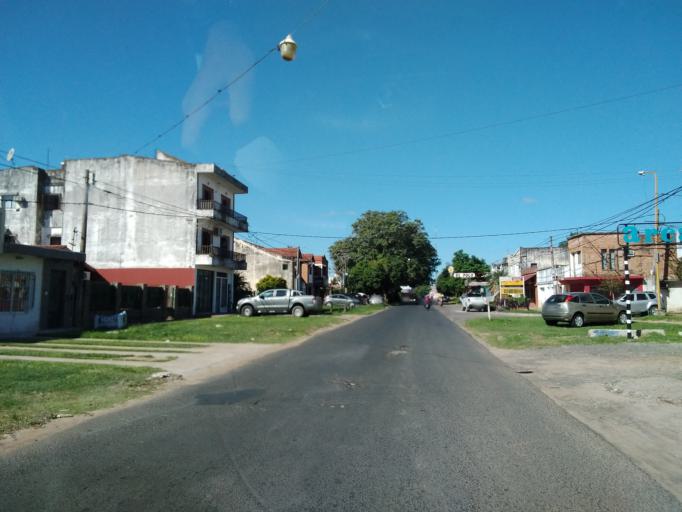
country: AR
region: Corrientes
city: Corrientes
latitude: -27.4707
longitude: -58.8158
